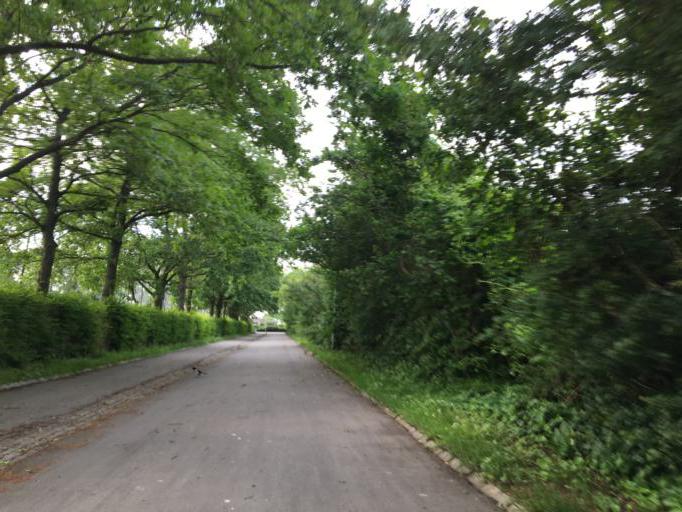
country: DK
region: Capital Region
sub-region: Tarnby Kommune
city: Tarnby
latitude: 55.6312
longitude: 12.6322
